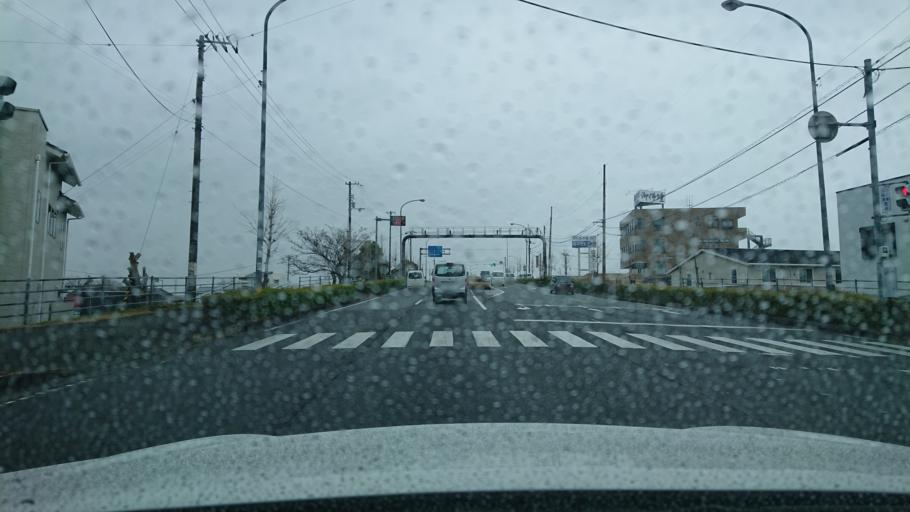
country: JP
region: Tokushima
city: Tokushima-shi
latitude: 34.0810
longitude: 134.5062
